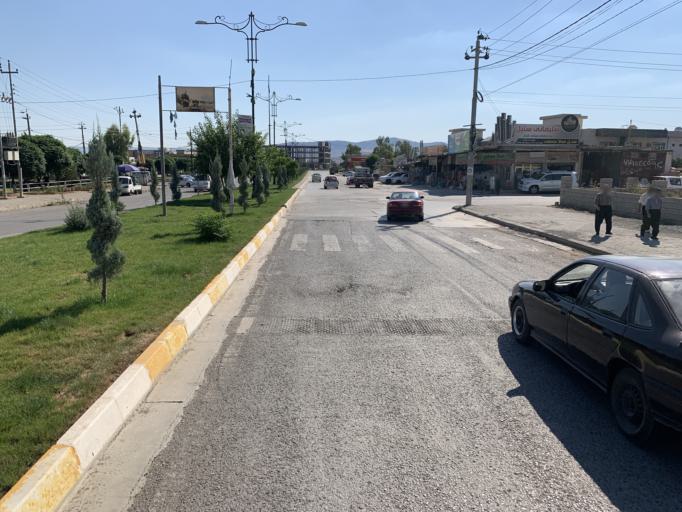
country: IQ
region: As Sulaymaniyah
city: Raniye
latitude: 36.2334
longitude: 44.7894
